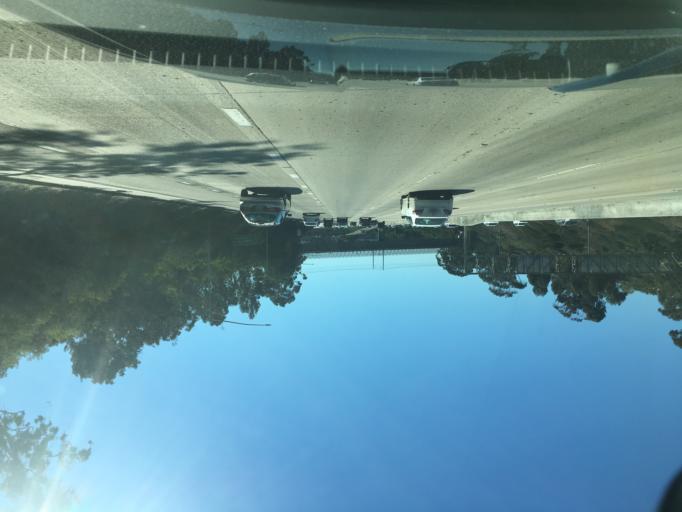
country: US
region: California
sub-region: San Diego County
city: National City
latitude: 32.7097
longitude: -117.0993
